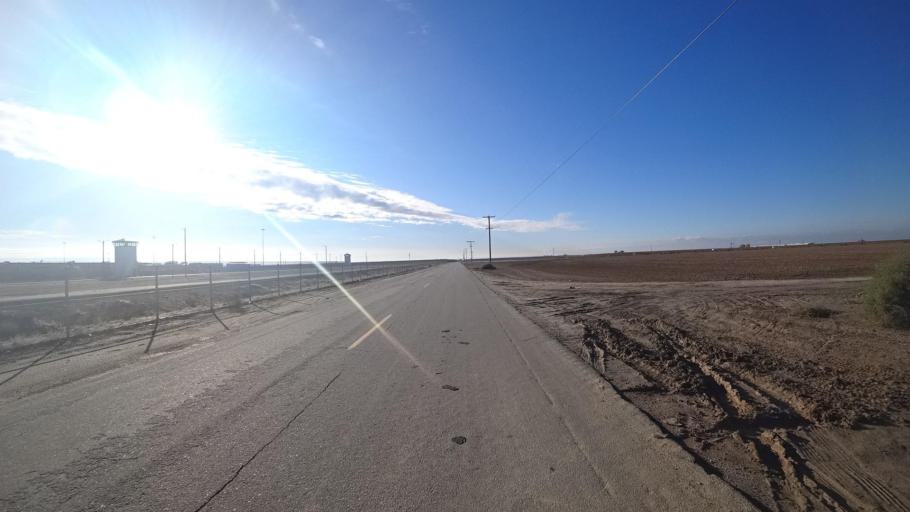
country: US
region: California
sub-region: Kern County
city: Delano
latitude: 35.7650
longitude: -119.3298
